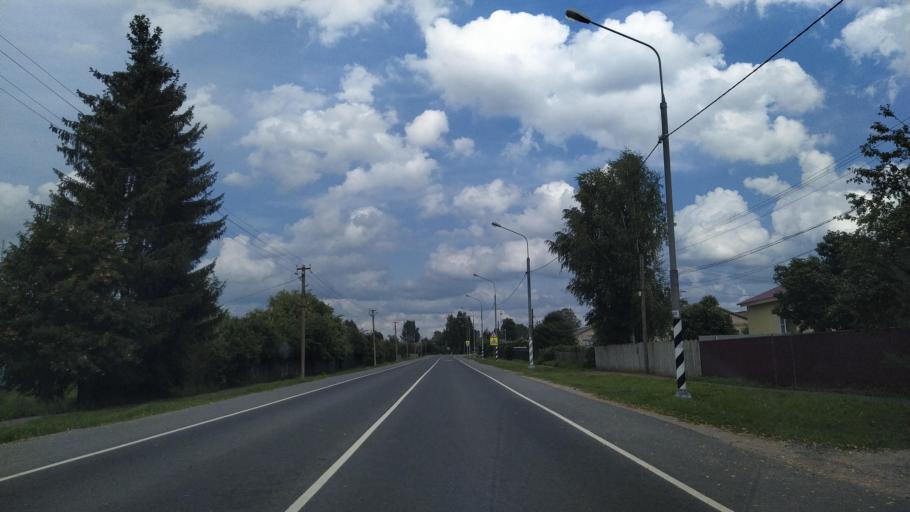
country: RU
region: Pskov
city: Dno
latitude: 58.0606
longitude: 29.9814
